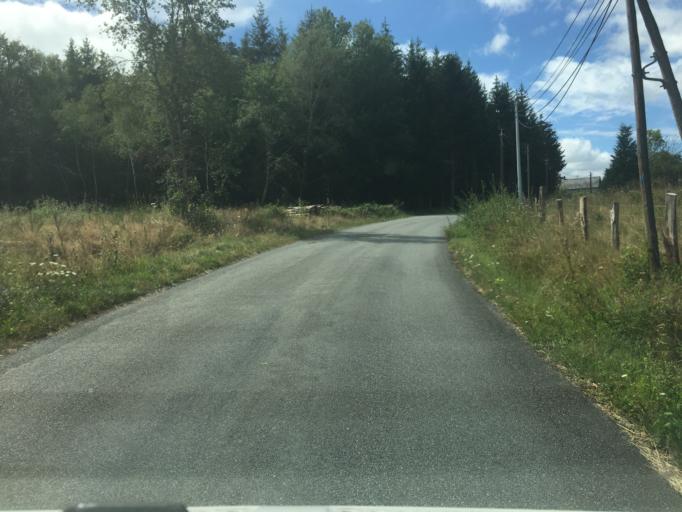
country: FR
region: Limousin
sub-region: Departement de la Correze
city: Neuvic
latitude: 45.4232
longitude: 2.3460
